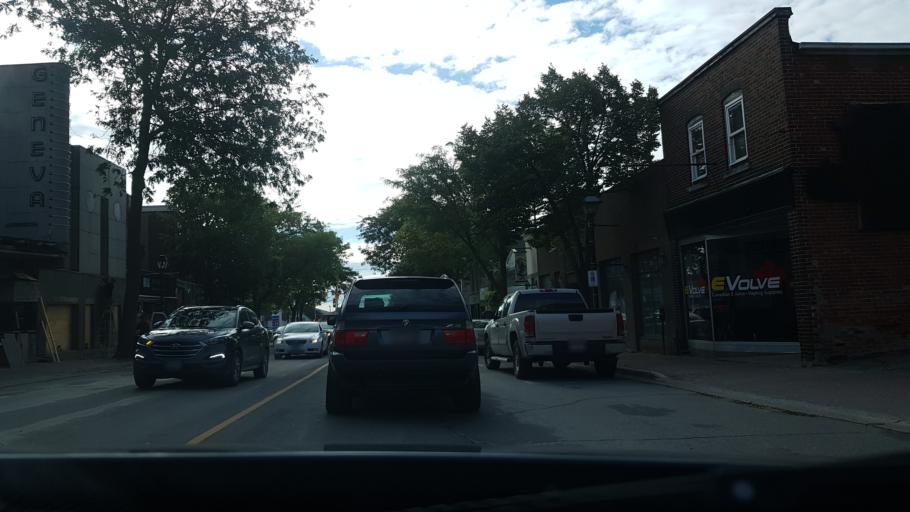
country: CA
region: Ontario
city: Orillia
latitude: 44.6081
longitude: -79.4196
